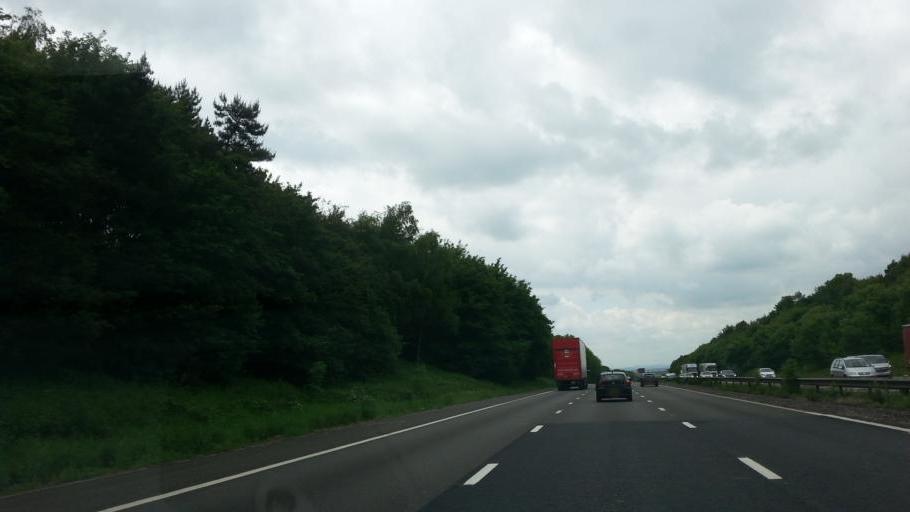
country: GB
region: England
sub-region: Solihull
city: Meriden
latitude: 52.4676
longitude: -1.6192
